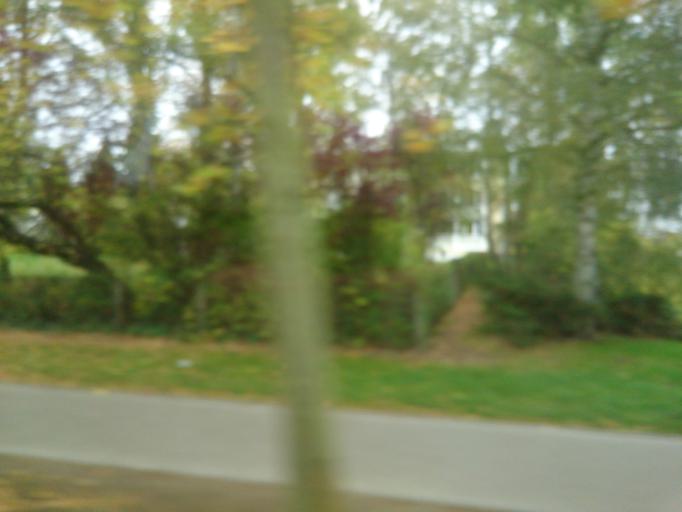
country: DE
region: Mecklenburg-Vorpommern
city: Rostock
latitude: 54.0782
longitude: 12.1156
